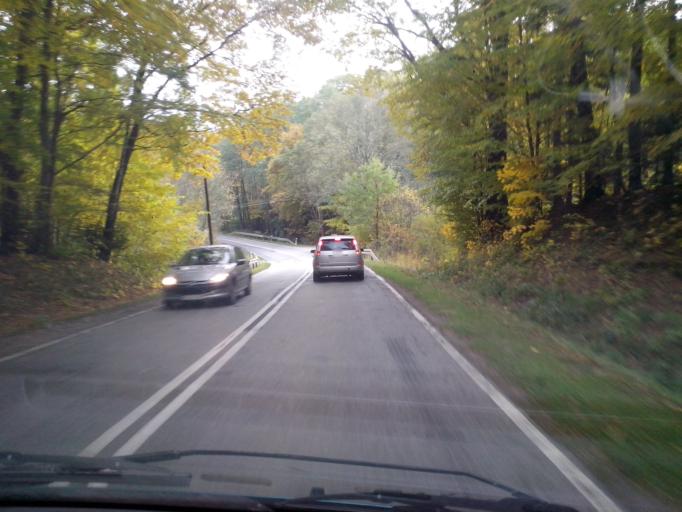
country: PL
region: Subcarpathian Voivodeship
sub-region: Powiat strzyzowski
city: Wisniowa
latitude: 49.8789
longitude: 21.6457
